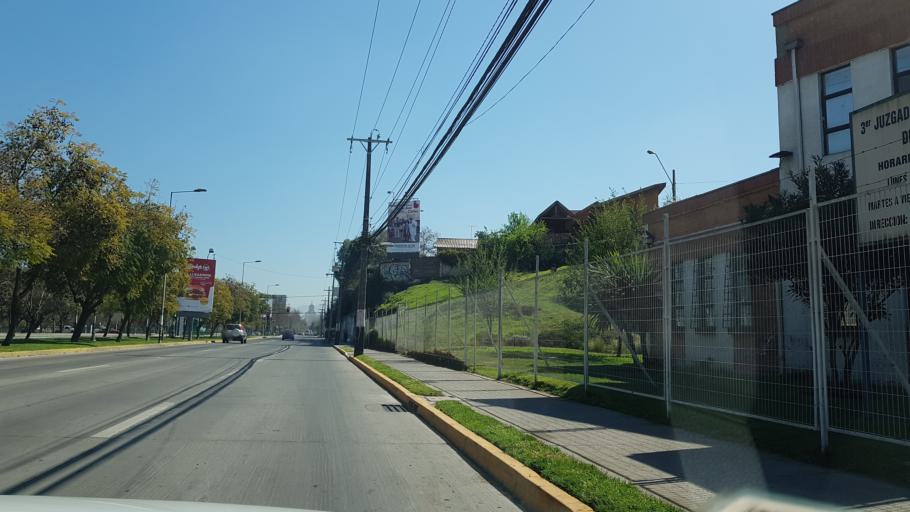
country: CL
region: Santiago Metropolitan
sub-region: Provincia de Santiago
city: Lo Prado
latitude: -33.5102
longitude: -70.7455
